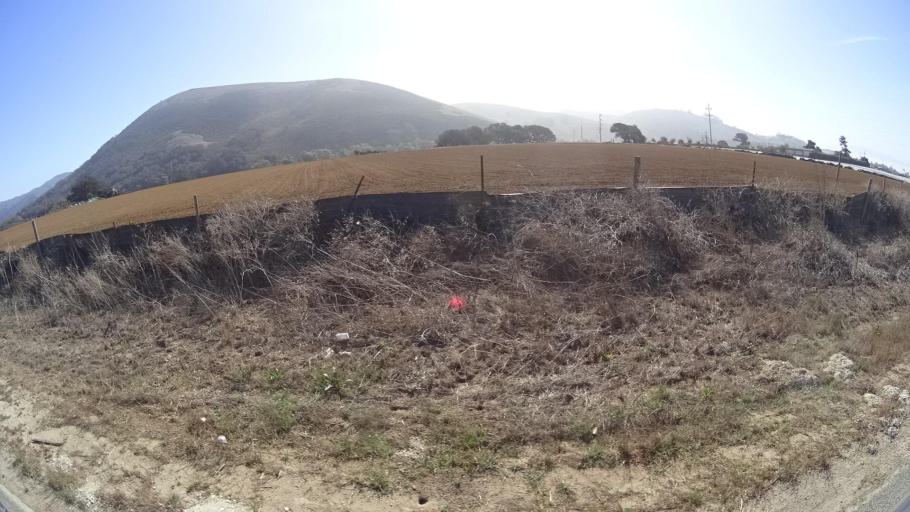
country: US
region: California
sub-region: Monterey County
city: Prunedale
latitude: 36.7696
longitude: -121.6082
